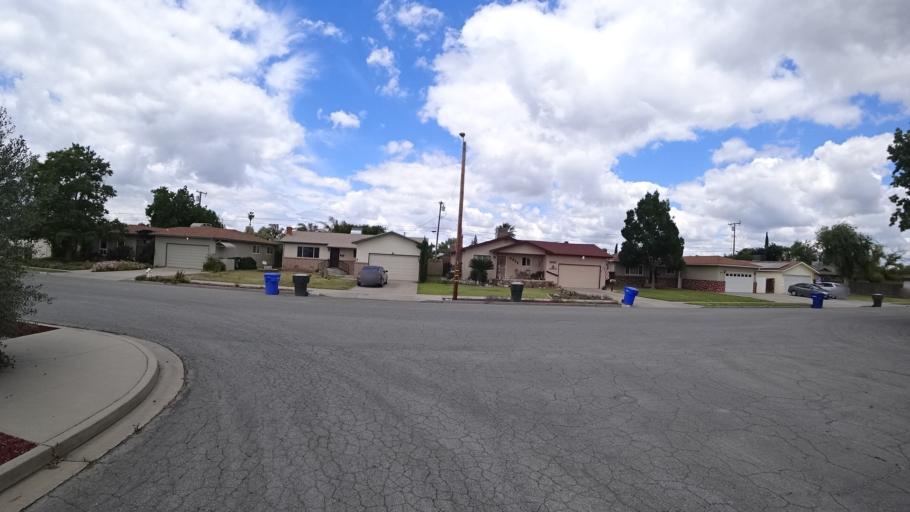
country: US
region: California
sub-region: Kings County
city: Hanford
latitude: 36.3479
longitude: -119.6388
